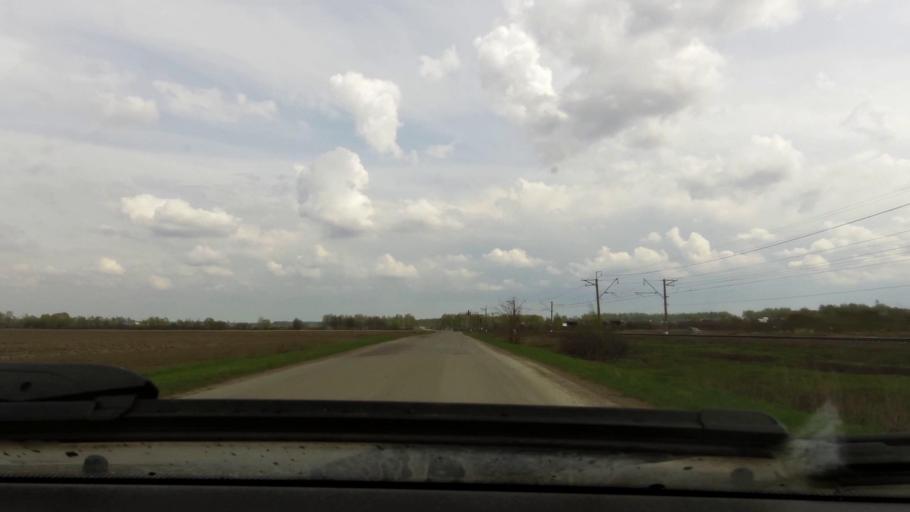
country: RU
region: Rjazan
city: Bagramovo
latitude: 54.7077
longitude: 39.3170
